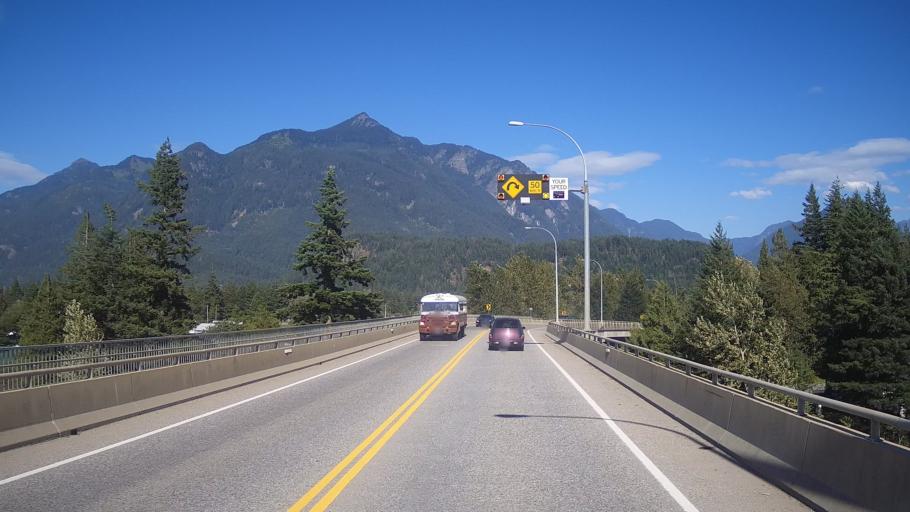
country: CA
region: British Columbia
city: Hope
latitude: 49.3864
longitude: -121.4514
